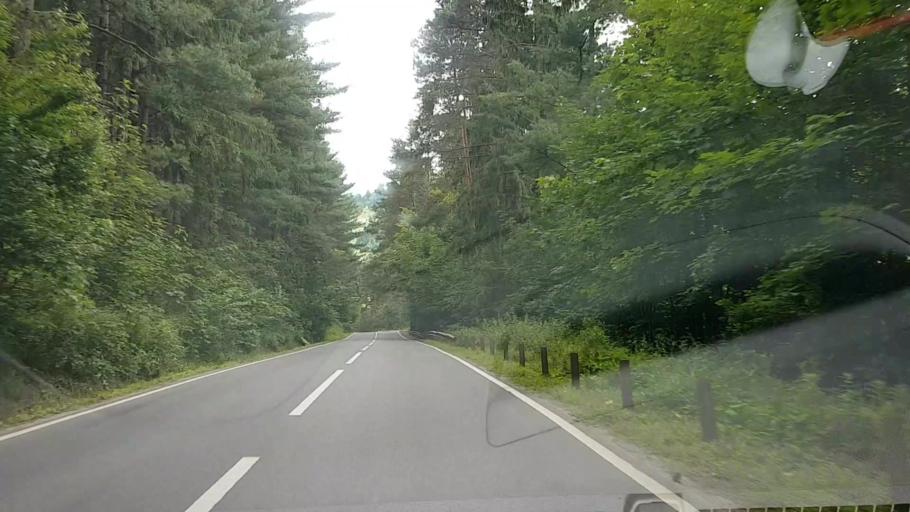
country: RO
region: Neamt
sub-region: Comuna Borca
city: Borca
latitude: 47.1735
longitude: 25.7934
